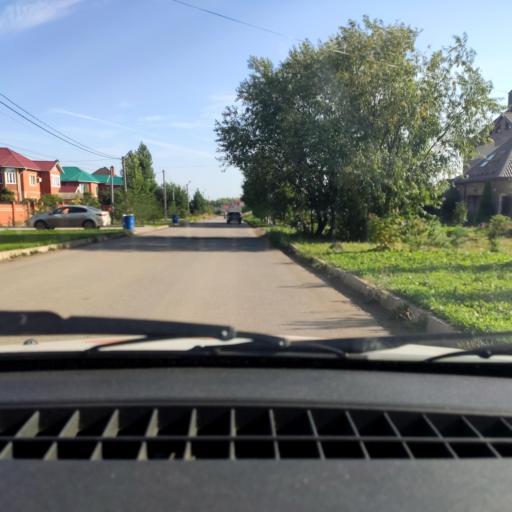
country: RU
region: Bashkortostan
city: Kabakovo
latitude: 54.6200
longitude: 56.1268
